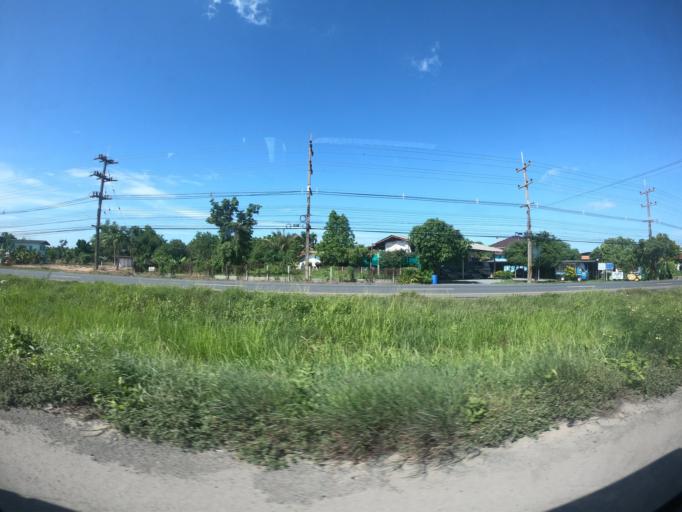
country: TH
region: Nakhon Nayok
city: Ban Na
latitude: 14.2480
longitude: 101.1051
